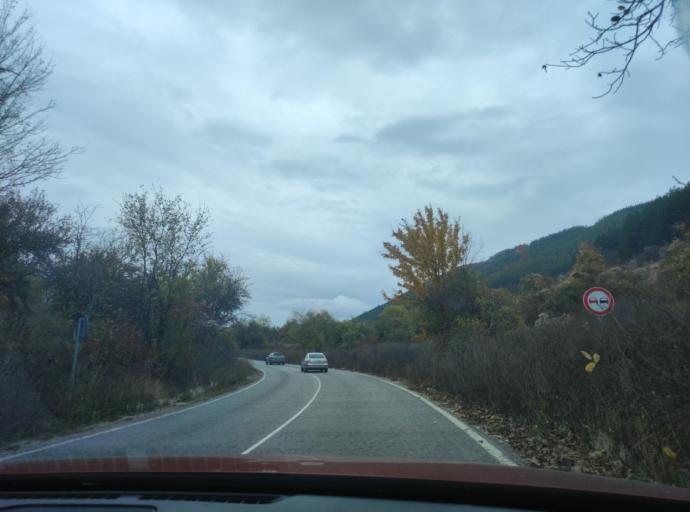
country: BG
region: Sofiya
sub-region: Obshtina Godech
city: Godech
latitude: 43.0330
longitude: 23.1362
